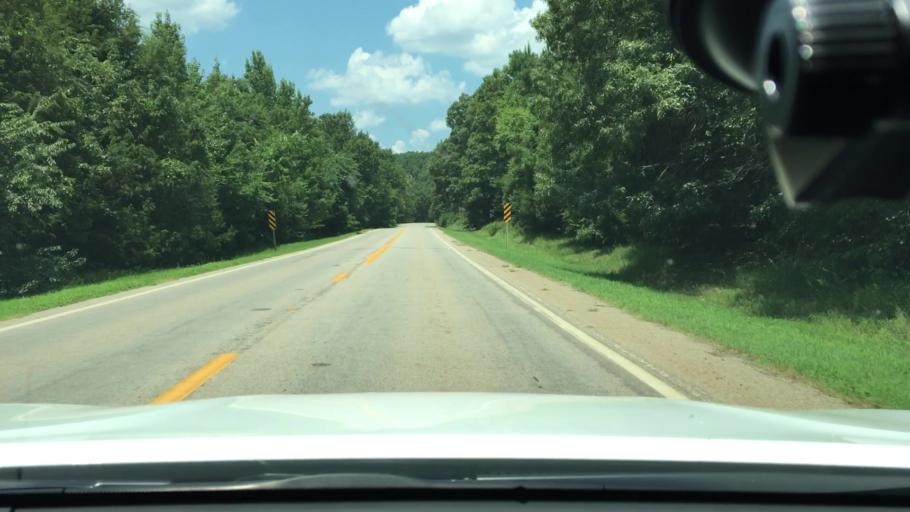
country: US
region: Arkansas
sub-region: Logan County
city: Booneville
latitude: 35.2130
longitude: -93.9361
